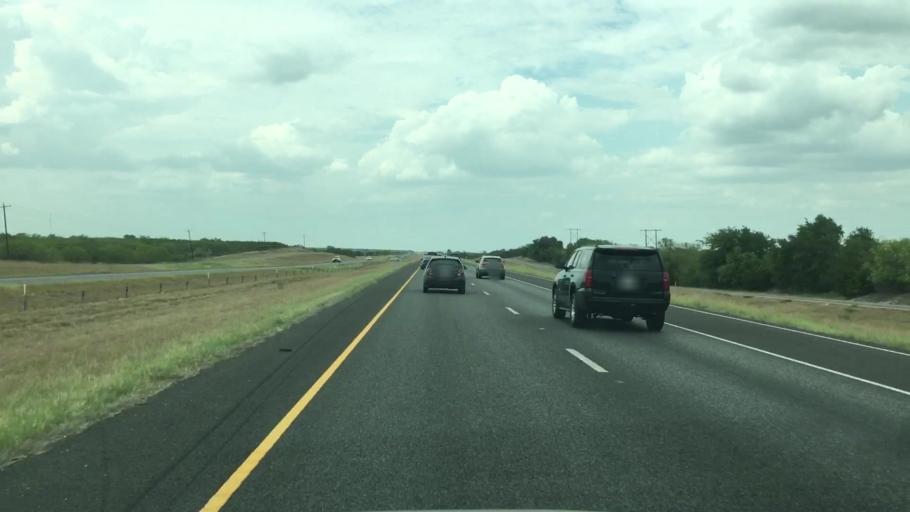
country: US
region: Texas
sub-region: Atascosa County
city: Pleasanton
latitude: 28.8341
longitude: -98.3711
